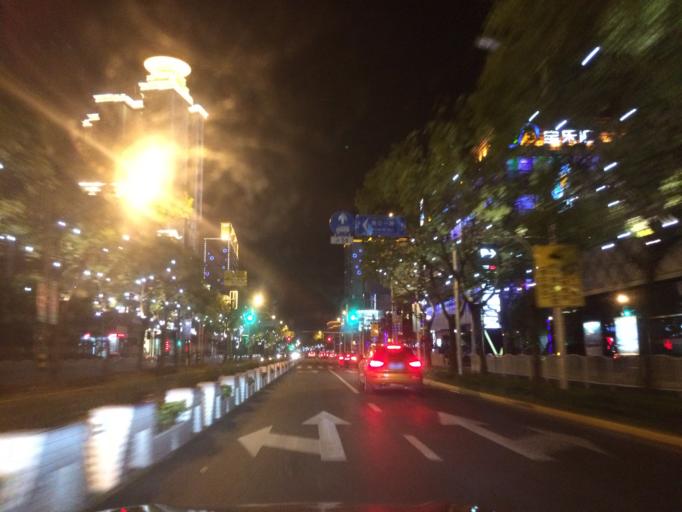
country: CN
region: Shanghai Shi
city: Baoshan
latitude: 31.4009
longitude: 121.4828
